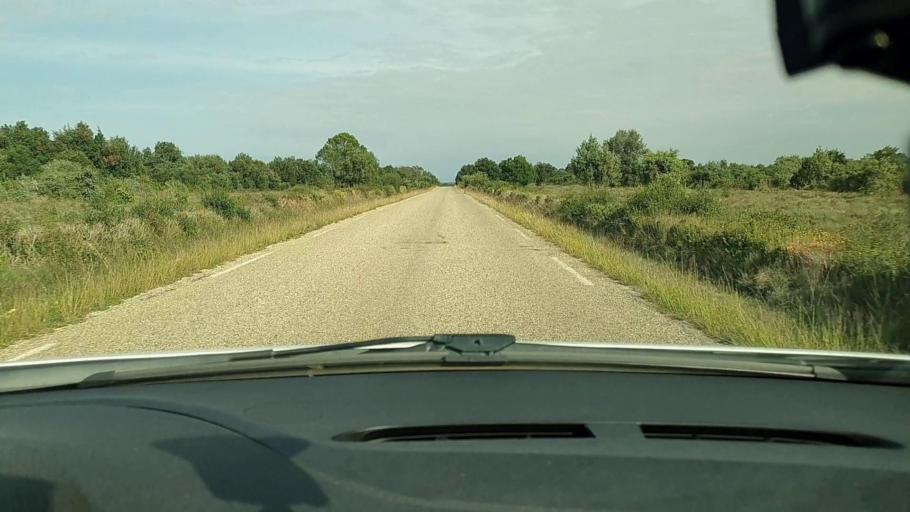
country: FR
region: Languedoc-Roussillon
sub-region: Departement du Gard
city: Saint-Quentin-la-Poterie
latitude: 44.1224
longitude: 4.4118
